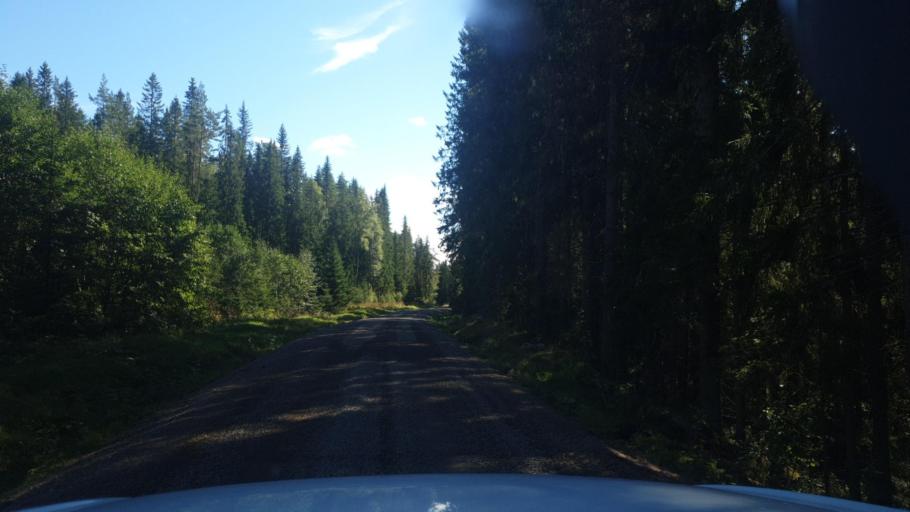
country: SE
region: Vaermland
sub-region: Eda Kommun
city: Charlottenberg
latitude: 60.0377
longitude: 12.5888
